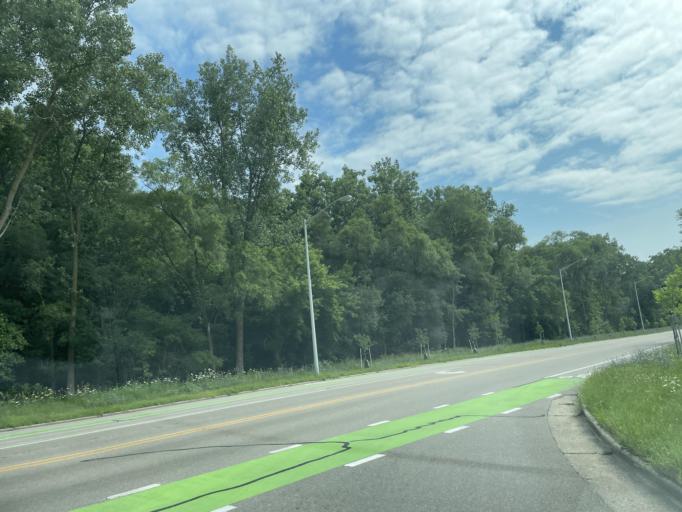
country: US
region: Michigan
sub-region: Kent County
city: East Grand Rapids
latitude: 42.9198
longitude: -85.6327
